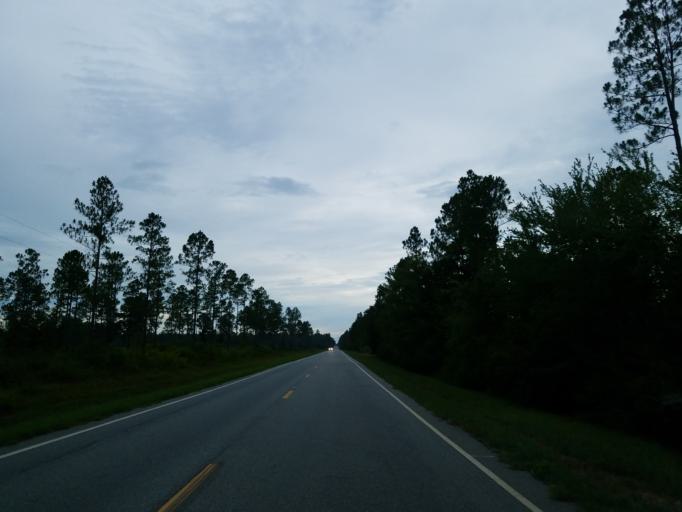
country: US
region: Georgia
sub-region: Lanier County
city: Lakeland
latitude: 30.9951
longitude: -83.0104
